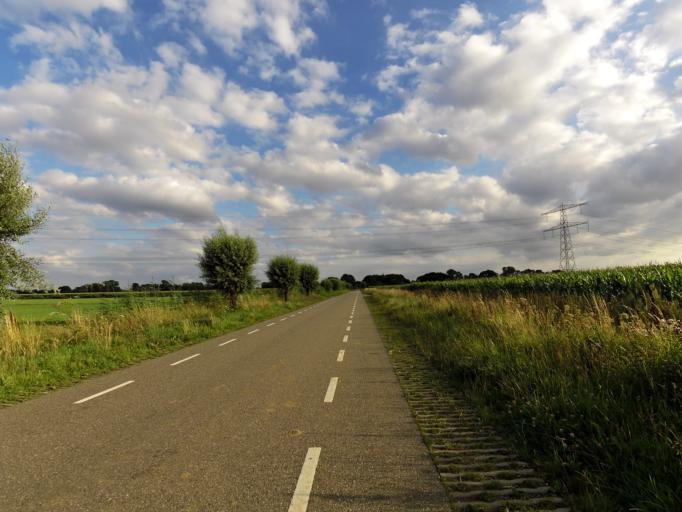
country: NL
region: Gelderland
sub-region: Gemeente Doesburg
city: Doesburg
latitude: 51.9777
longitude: 6.1615
